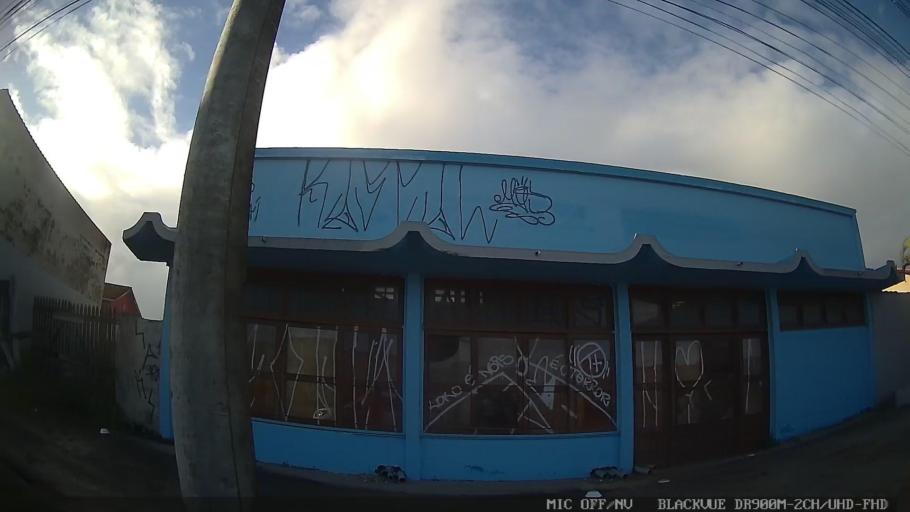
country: BR
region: Sao Paulo
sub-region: Itanhaem
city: Itanhaem
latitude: -24.2353
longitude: -46.9030
